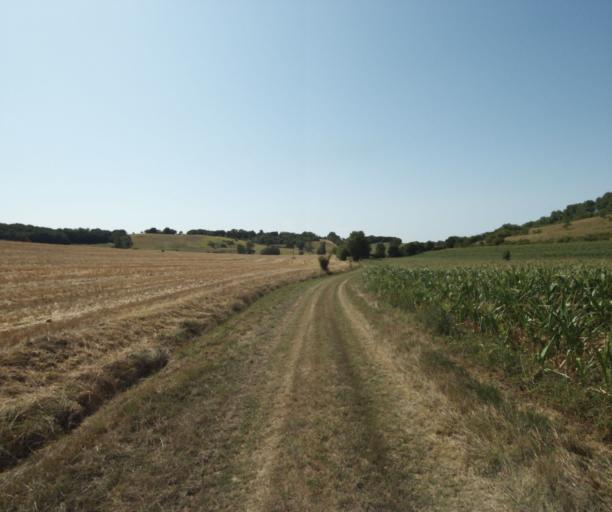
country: FR
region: Midi-Pyrenees
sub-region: Departement de la Haute-Garonne
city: Saint-Felix-Lauragais
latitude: 43.4533
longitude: 1.8666
